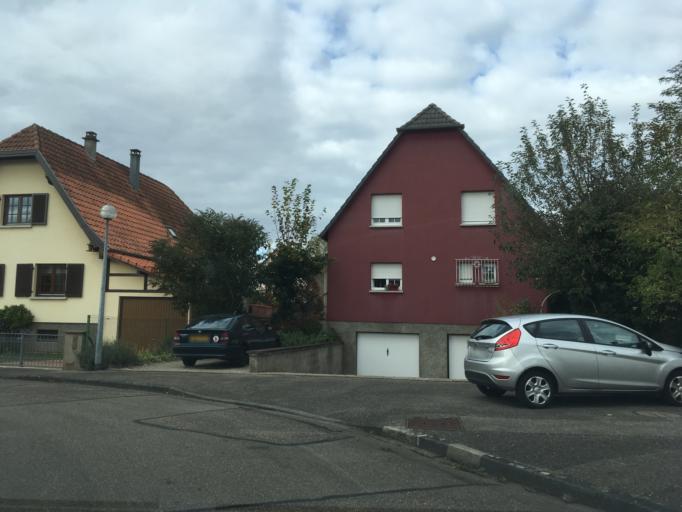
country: FR
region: Alsace
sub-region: Departement du Bas-Rhin
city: Illkirch-Graffenstaden
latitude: 48.5274
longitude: 7.7594
